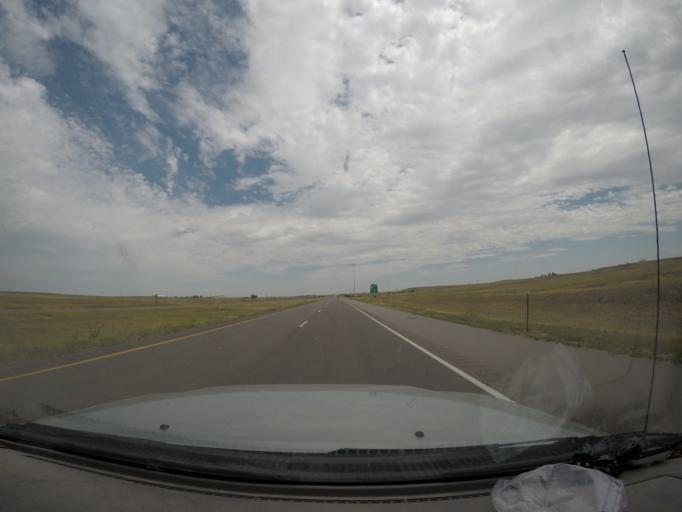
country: US
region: Nebraska
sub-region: Kimball County
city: Kimball
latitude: 41.2150
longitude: -103.6750
